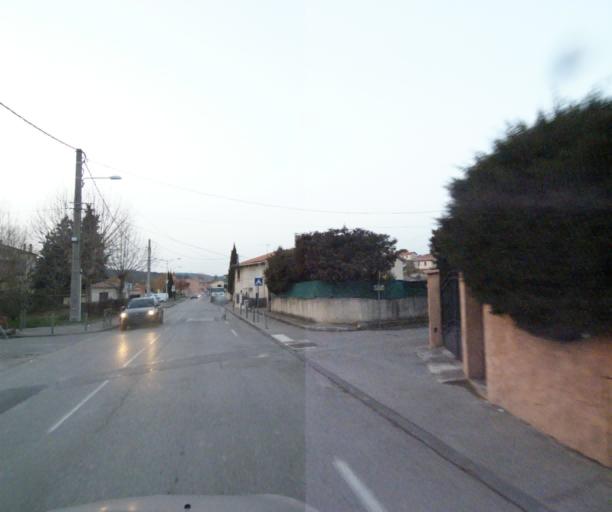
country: FR
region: Provence-Alpes-Cote d'Azur
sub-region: Departement des Bouches-du-Rhone
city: Gardanne
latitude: 43.4320
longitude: 5.4675
